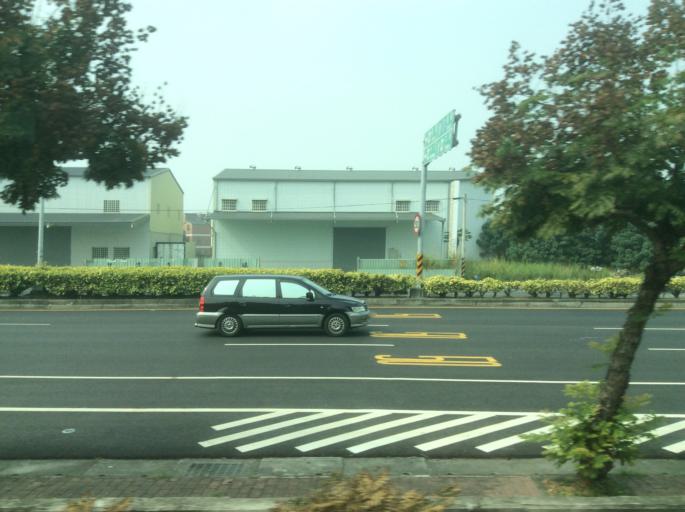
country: TW
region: Taiwan
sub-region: Chiayi
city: Taibao
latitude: 23.4261
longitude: 120.3936
